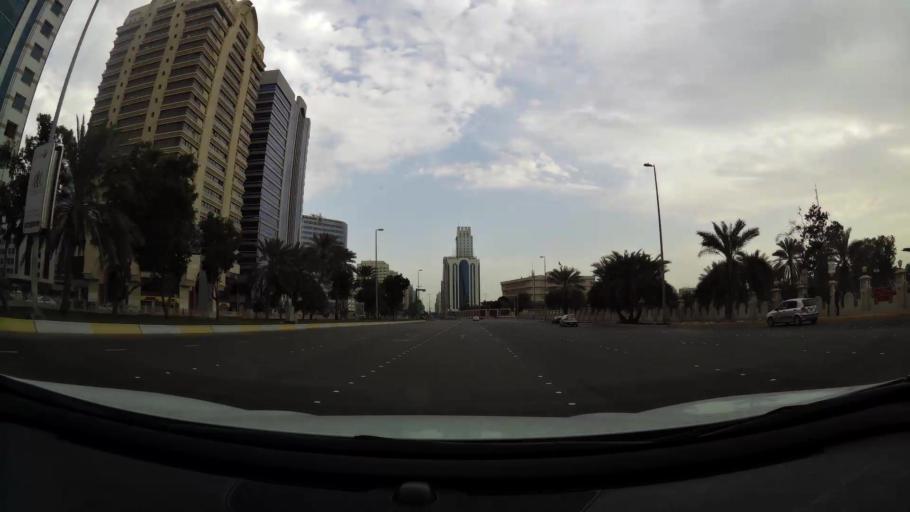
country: AE
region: Abu Dhabi
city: Abu Dhabi
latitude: 24.4773
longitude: 54.3638
